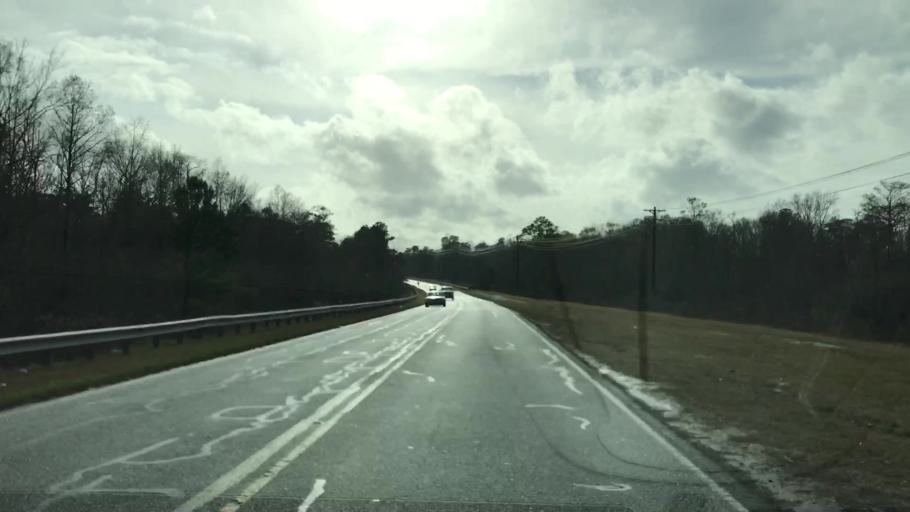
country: US
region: South Carolina
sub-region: Williamsburg County
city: Andrews
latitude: 33.4872
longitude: -79.5494
